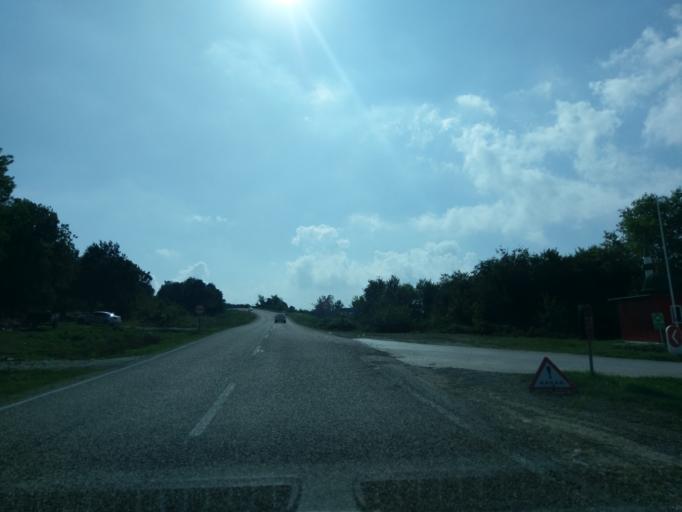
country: TR
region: Sinop
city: Erfelek
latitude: 41.9754
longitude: 34.8683
